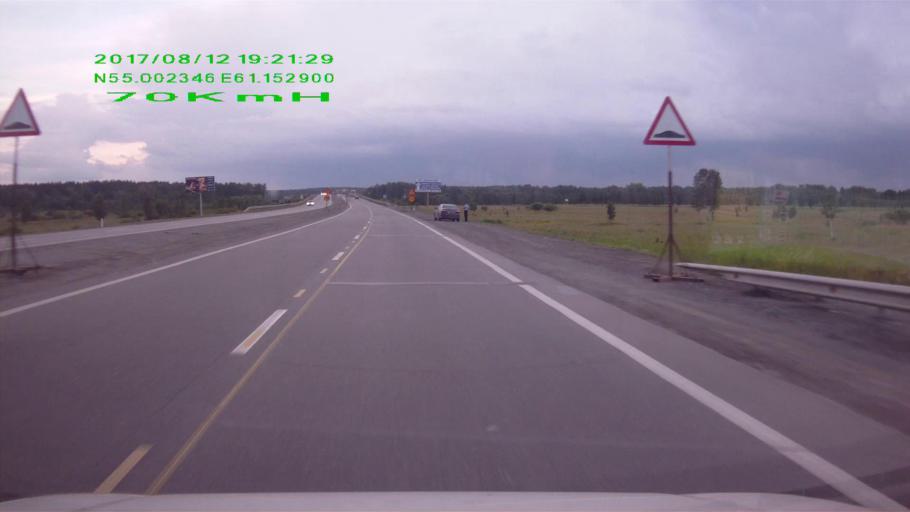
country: RU
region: Chelyabinsk
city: Poletayevo
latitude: 55.0012
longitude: 61.1499
